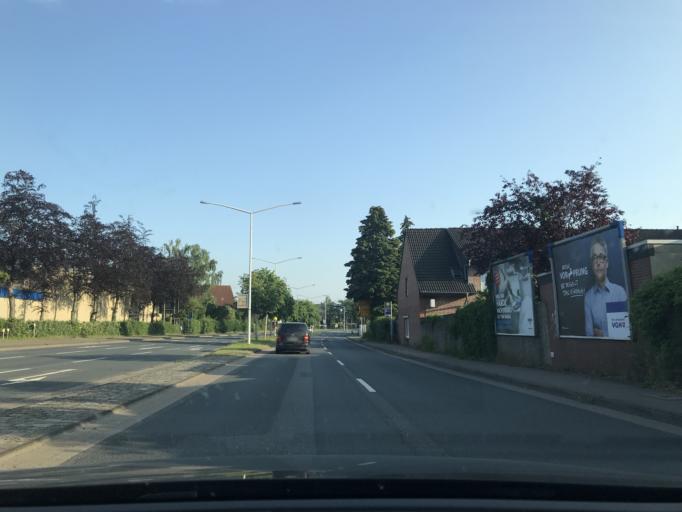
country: DE
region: Lower Saxony
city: Lehrte
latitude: 52.3722
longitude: 9.9769
